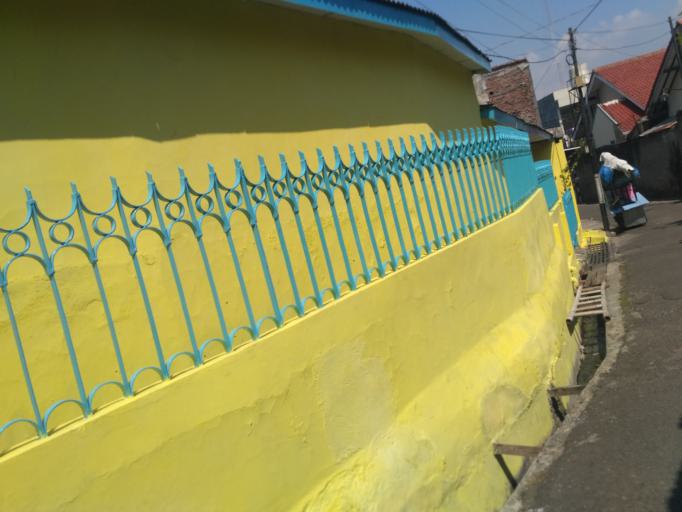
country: ID
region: Central Java
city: Semarang
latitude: -7.0001
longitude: 110.4313
